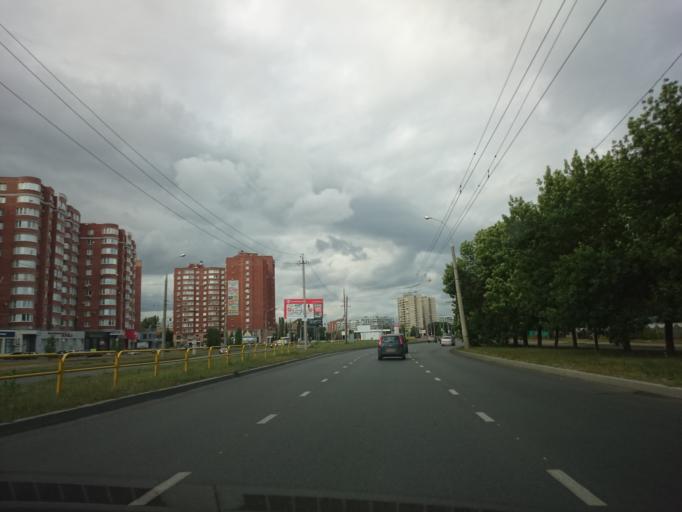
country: RU
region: Samara
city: Tol'yatti
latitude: 53.5138
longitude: 49.3071
